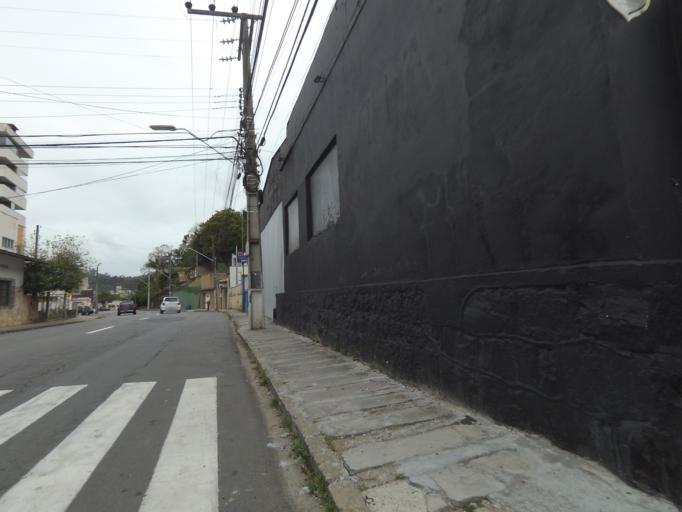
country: BR
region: Santa Catarina
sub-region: Blumenau
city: Blumenau
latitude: -26.9156
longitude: -49.0821
